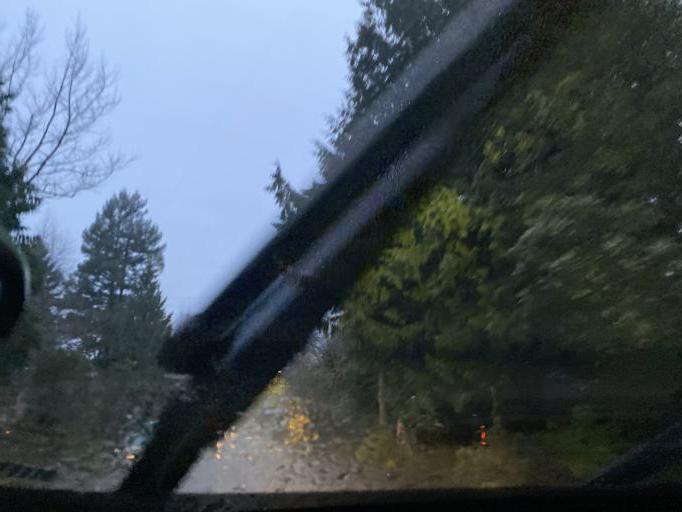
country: US
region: Washington
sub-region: King County
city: Seattle
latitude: 47.6570
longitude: -122.3958
